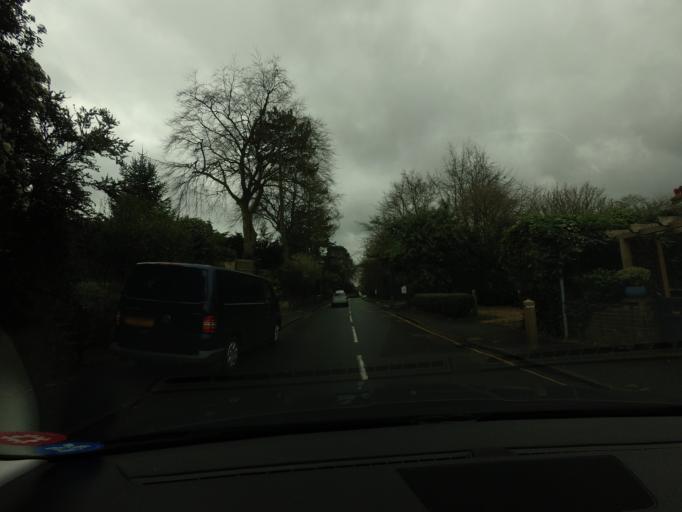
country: GB
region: England
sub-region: Kent
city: Eynsford
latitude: 51.3717
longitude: 0.2176
